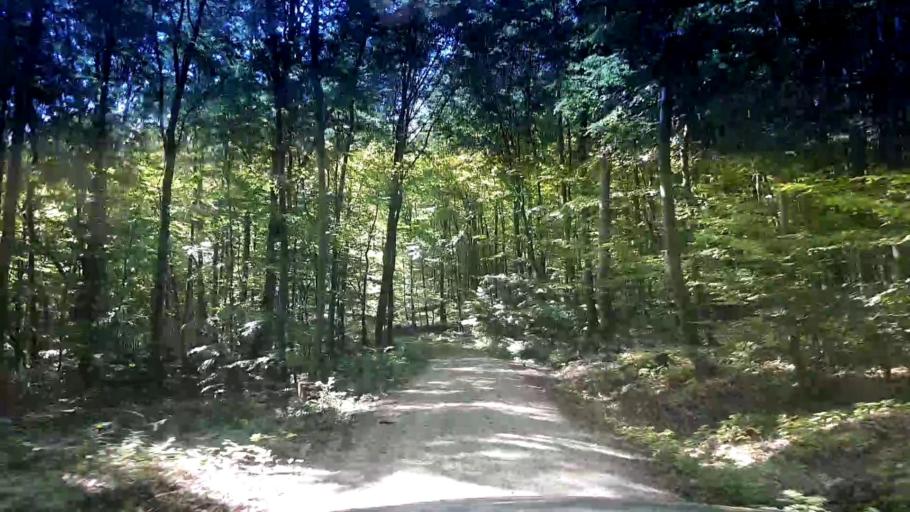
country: DE
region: Bavaria
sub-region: Upper Franconia
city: Litzendorf
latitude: 49.8840
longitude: 11.0504
